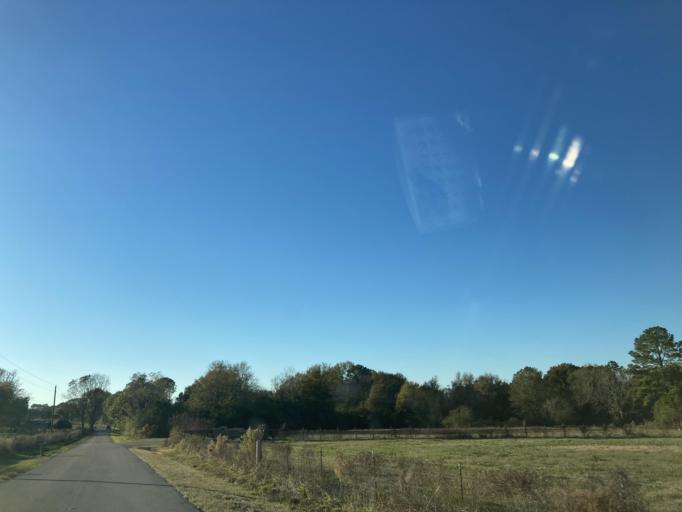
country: US
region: Mississippi
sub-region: Lamar County
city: Sumrall
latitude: 31.2680
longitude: -89.5953
